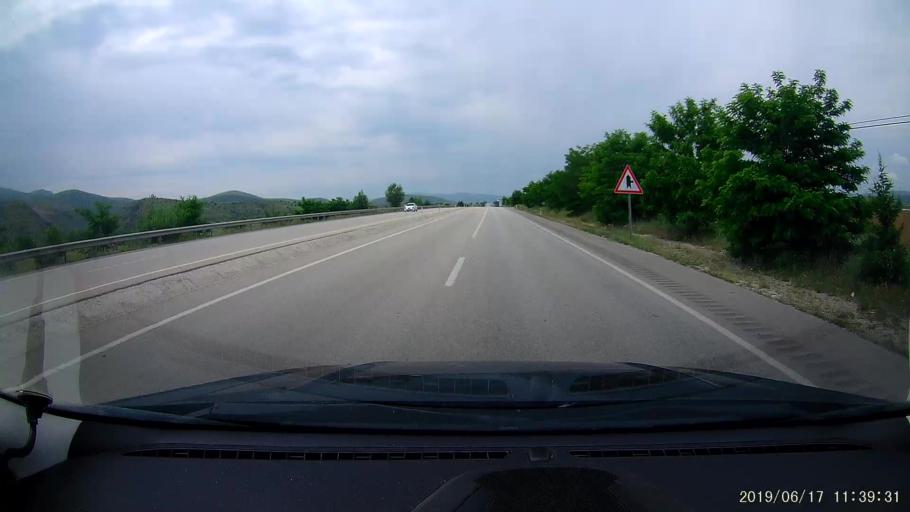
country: TR
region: Cankiri
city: Kursunlu
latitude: 40.8398
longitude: 33.3735
